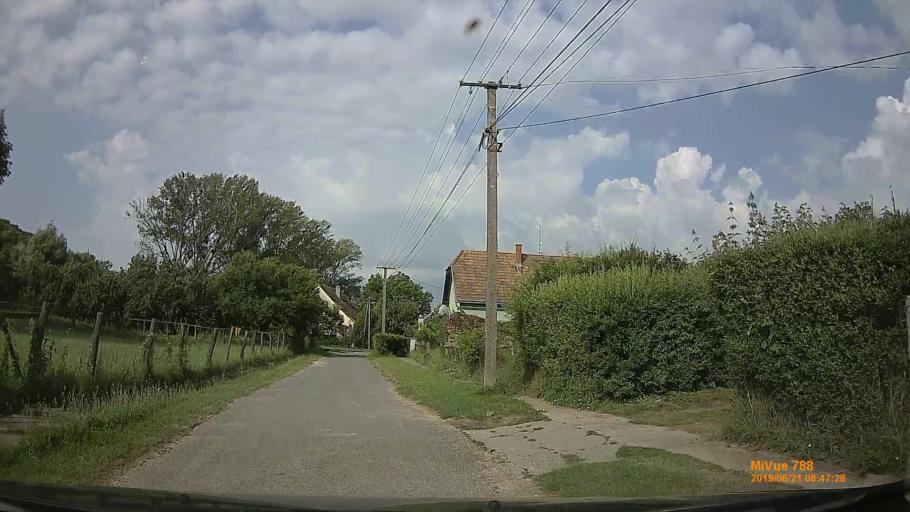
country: HU
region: Baranya
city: Buekkoesd
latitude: 46.1901
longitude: 17.9323
